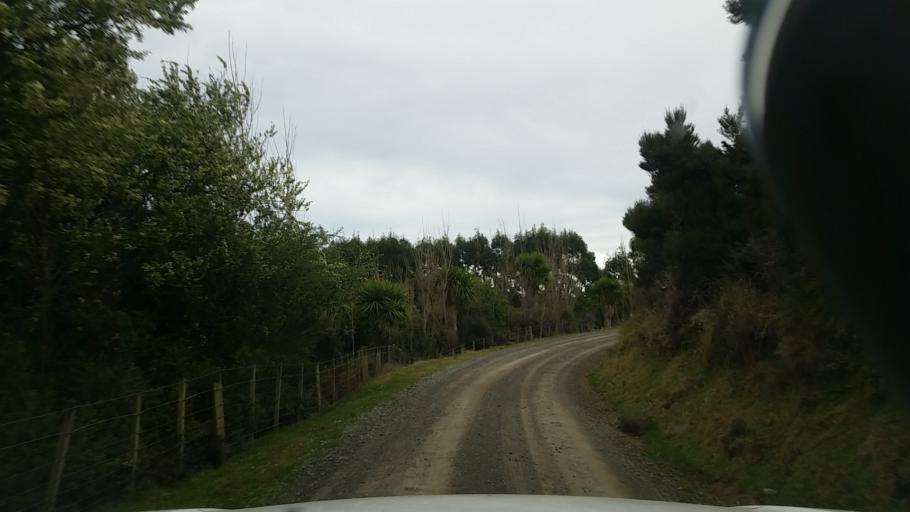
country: NZ
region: Canterbury
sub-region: Christchurch City
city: Christchurch
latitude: -43.8582
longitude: 173.0222
